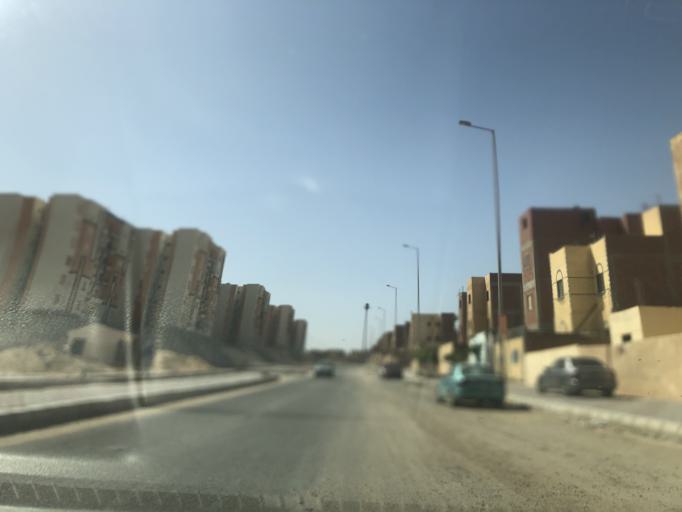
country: EG
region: Al Jizah
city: Madinat Sittah Uktubar
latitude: 29.9339
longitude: 30.9818
